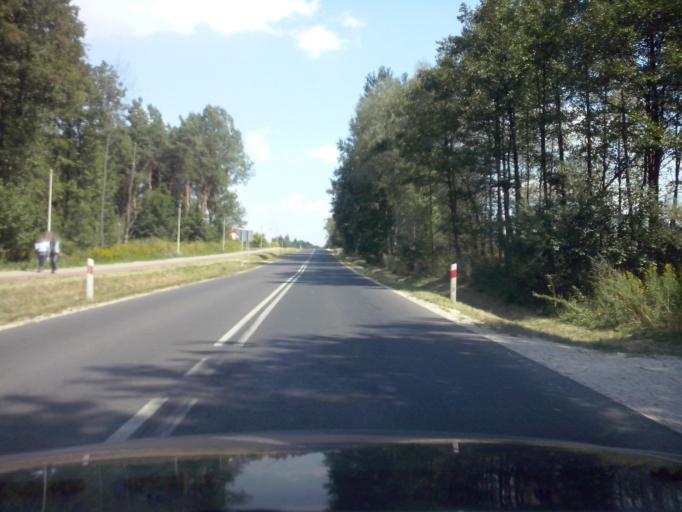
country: PL
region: Swietokrzyskie
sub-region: Powiat staszowski
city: Staszow
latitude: 50.5568
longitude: 21.1916
